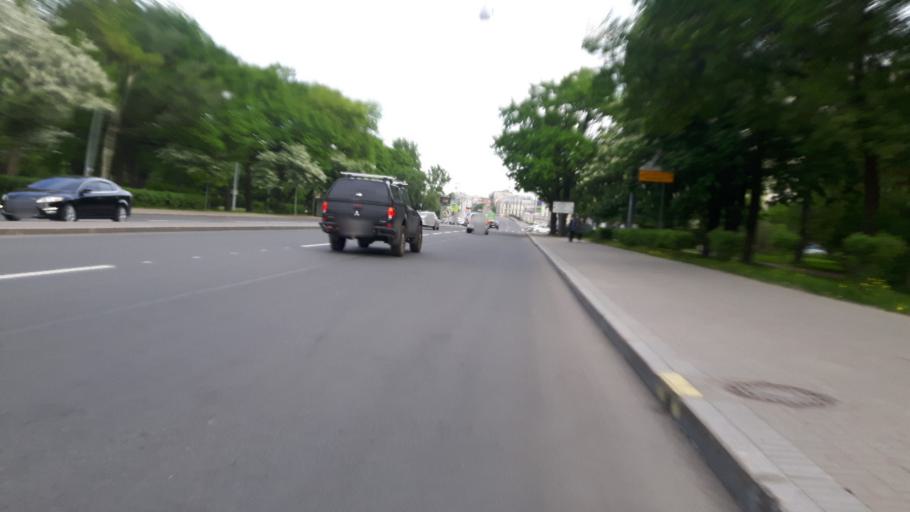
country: RU
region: Leningrad
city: Krestovskiy ostrov
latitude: 59.9694
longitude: 30.2761
